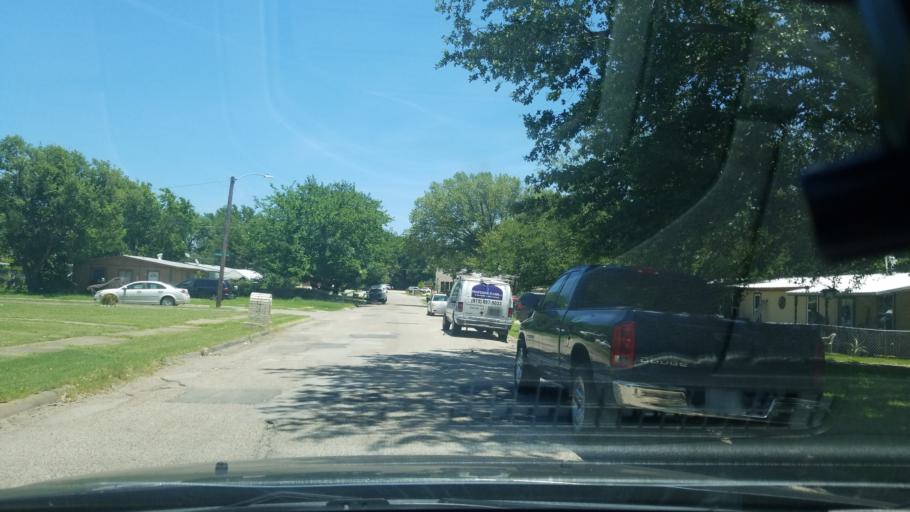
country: US
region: Texas
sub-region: Dallas County
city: Mesquite
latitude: 32.7801
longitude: -96.6019
